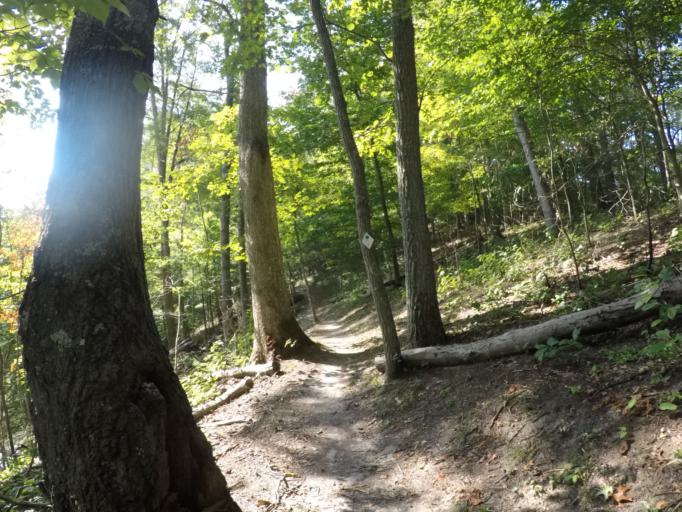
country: US
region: Ohio
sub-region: Lawrence County
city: Ironton
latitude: 38.6174
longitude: -82.6257
